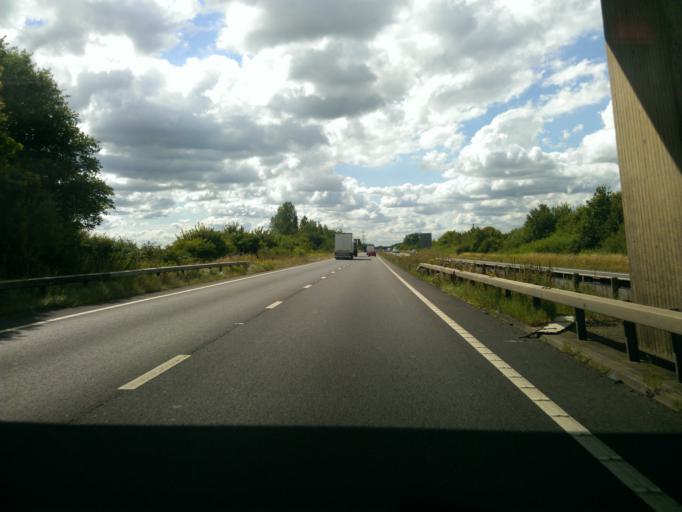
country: GB
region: England
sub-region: Northamptonshire
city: Long Buckby
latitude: 52.3927
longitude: -1.1071
